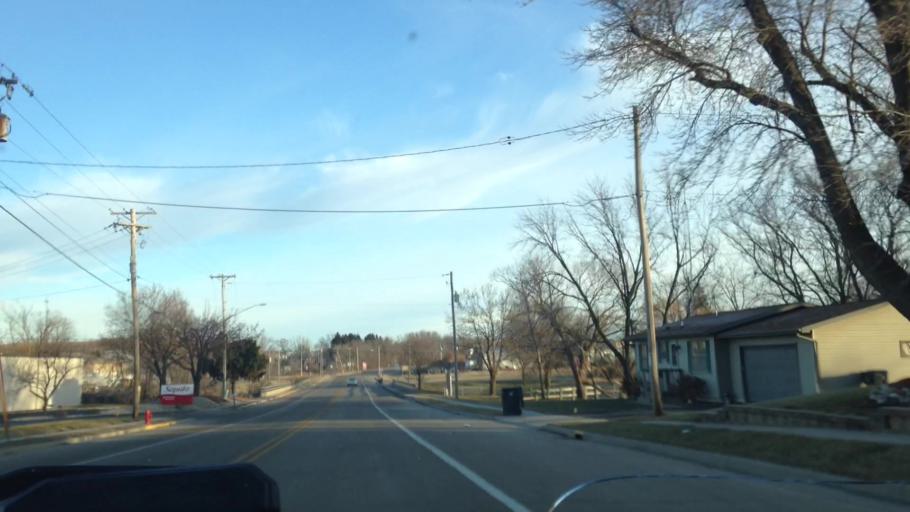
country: US
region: Wisconsin
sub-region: Dodge County
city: Mayville
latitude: 43.5059
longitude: -88.5424
